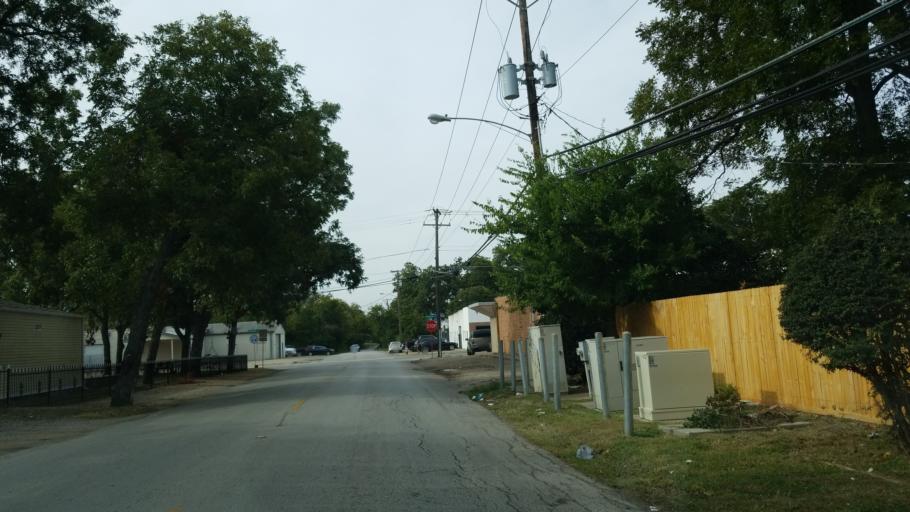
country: US
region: Texas
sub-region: Dallas County
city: Dallas
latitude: 32.7814
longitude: -96.7181
